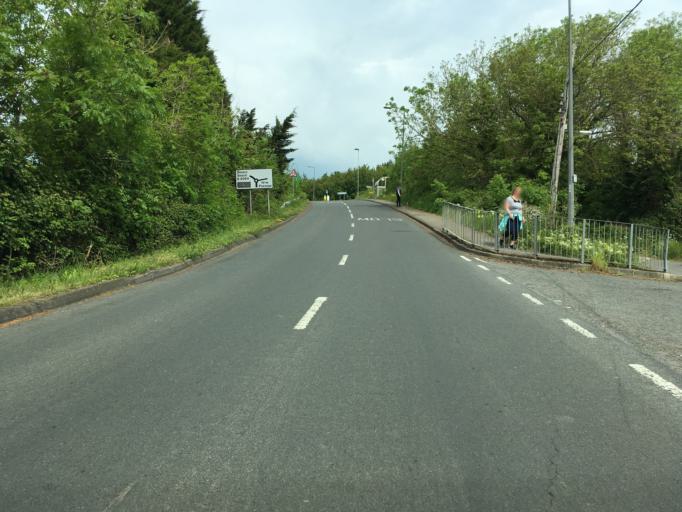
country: GB
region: England
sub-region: South Gloucestershire
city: Severn Beach
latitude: 51.5677
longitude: -2.6498
